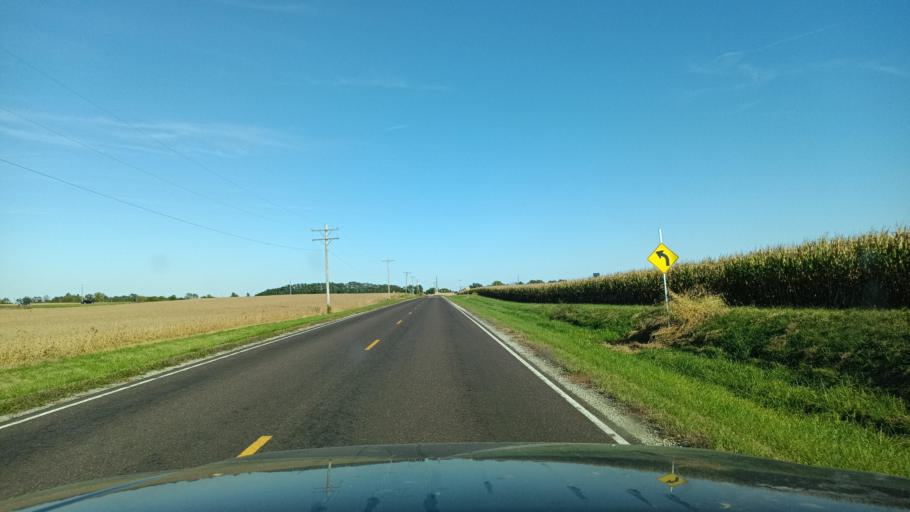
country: US
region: Illinois
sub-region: De Witt County
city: Clinton
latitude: 40.2315
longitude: -88.9753
